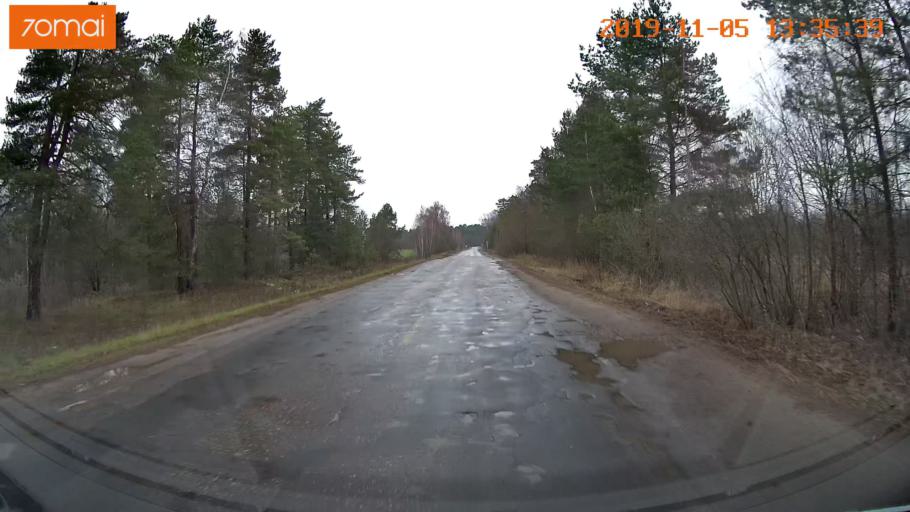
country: RU
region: Ivanovo
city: Shuya
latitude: 56.9094
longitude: 41.3862
